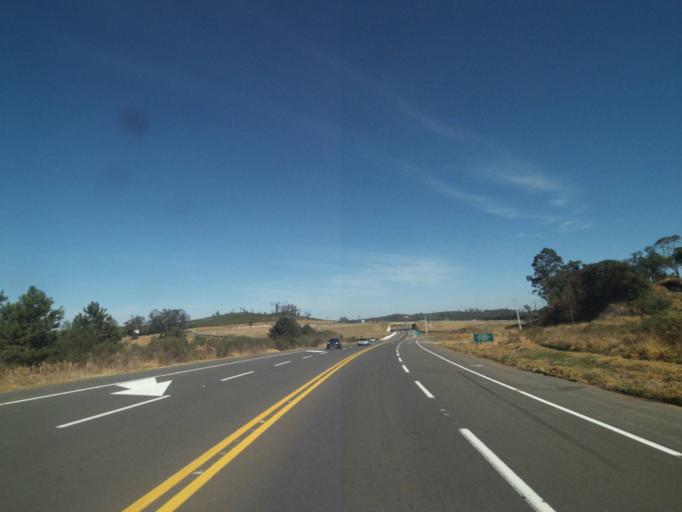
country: BR
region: Parana
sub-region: Tibagi
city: Tibagi
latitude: -24.8130
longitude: -50.4842
